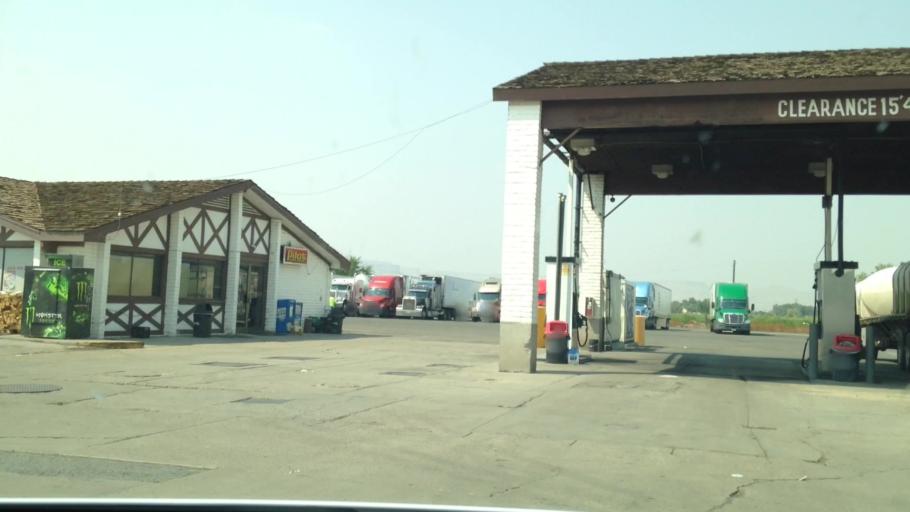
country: US
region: Utah
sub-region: Carbon County
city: East Carbon City
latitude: 38.9954
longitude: -110.1487
